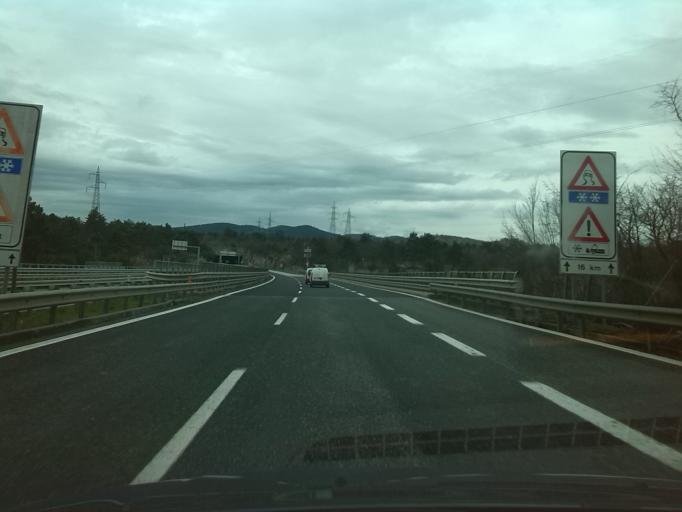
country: IT
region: Friuli Venezia Giulia
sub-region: Provincia di Trieste
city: Villa Opicina
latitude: 45.6949
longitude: 13.8069
